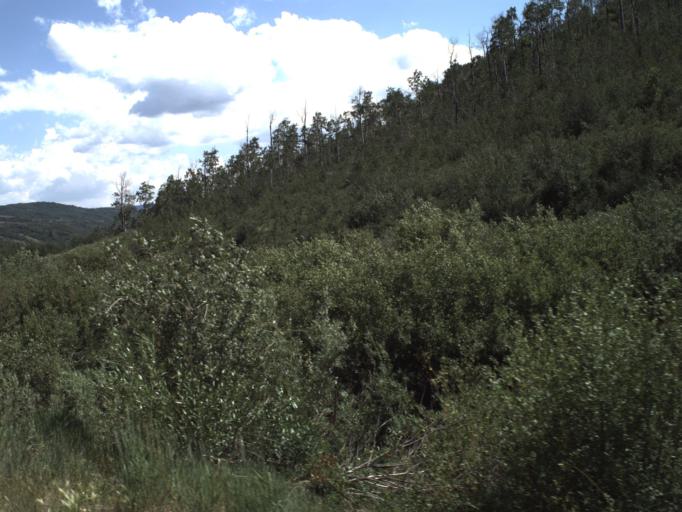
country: US
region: Utah
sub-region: Weber County
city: Wolf Creek
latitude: 41.3962
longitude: -111.5999
